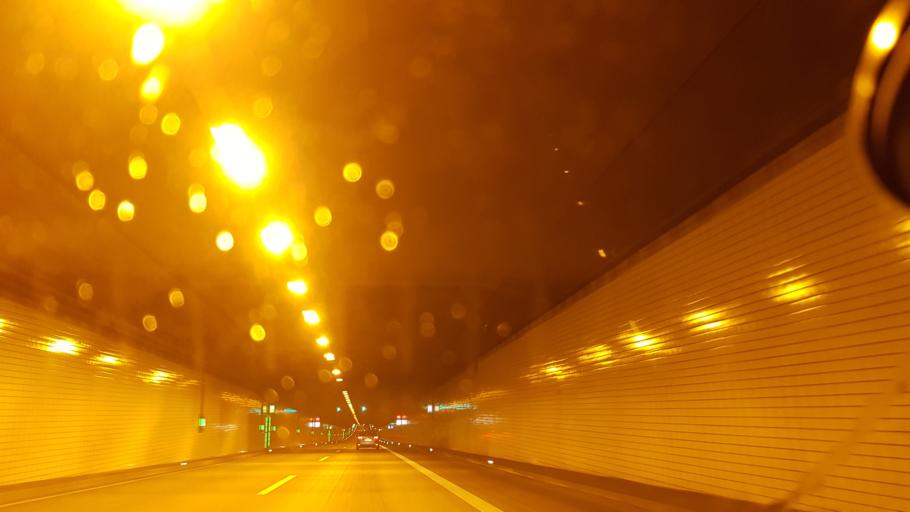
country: DE
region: Lower Saxony
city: Jemgum
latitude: 53.2304
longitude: 7.3990
